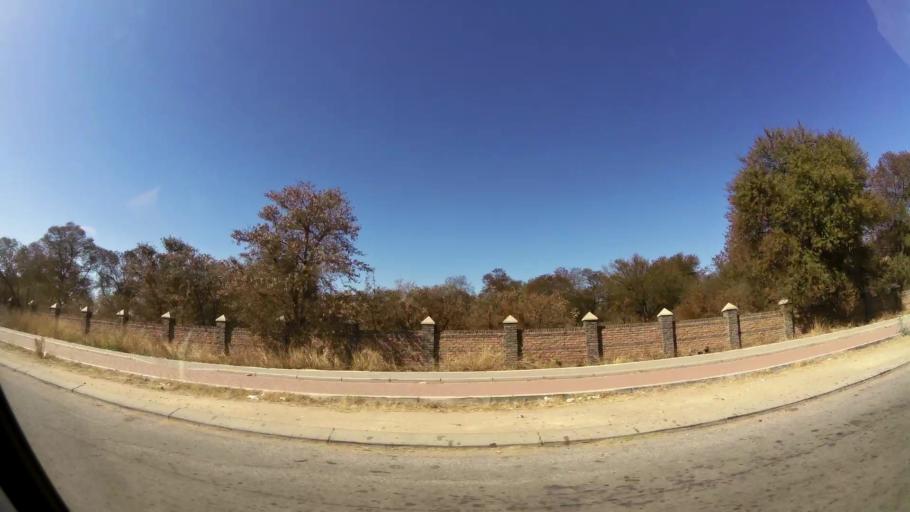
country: ZA
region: Limpopo
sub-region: Capricorn District Municipality
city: Polokwane
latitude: -23.8889
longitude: 29.4248
